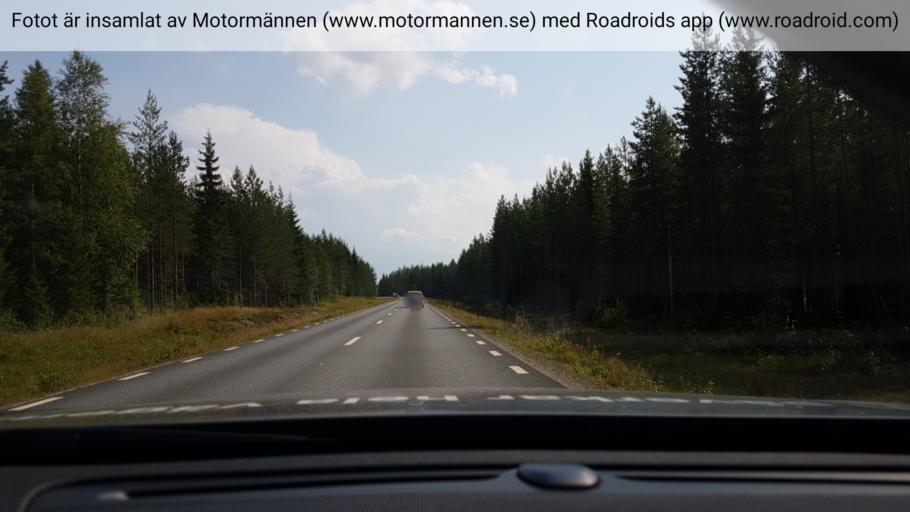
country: SE
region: Vaesterbotten
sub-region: Bjurholms Kommun
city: Bjurholm
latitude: 64.3200
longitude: 19.1583
